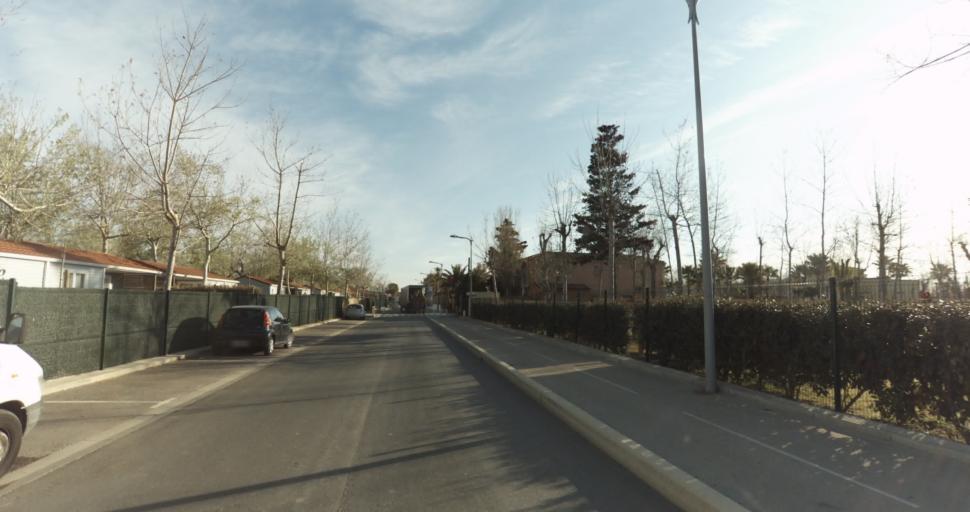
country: FR
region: Languedoc-Roussillon
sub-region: Departement de l'Herault
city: Le Cap d'Agde
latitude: 43.3089
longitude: 3.5418
